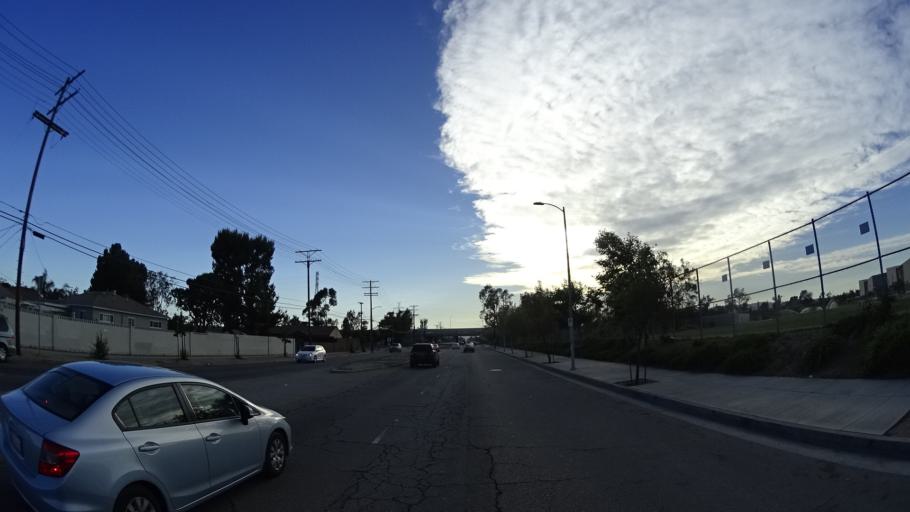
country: US
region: California
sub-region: Los Angeles County
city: Van Nuys
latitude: 34.2217
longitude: -118.4072
